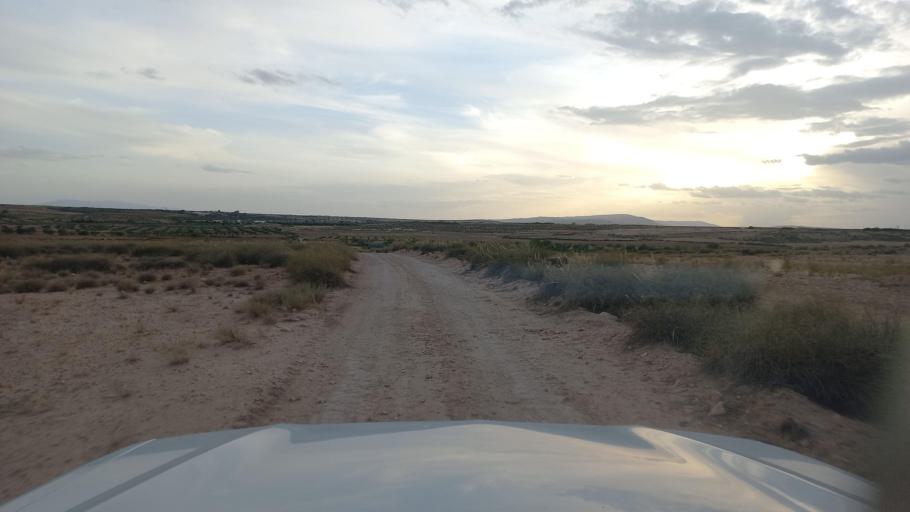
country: TN
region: Al Qasrayn
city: Sbiba
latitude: 35.4169
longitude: 9.0874
